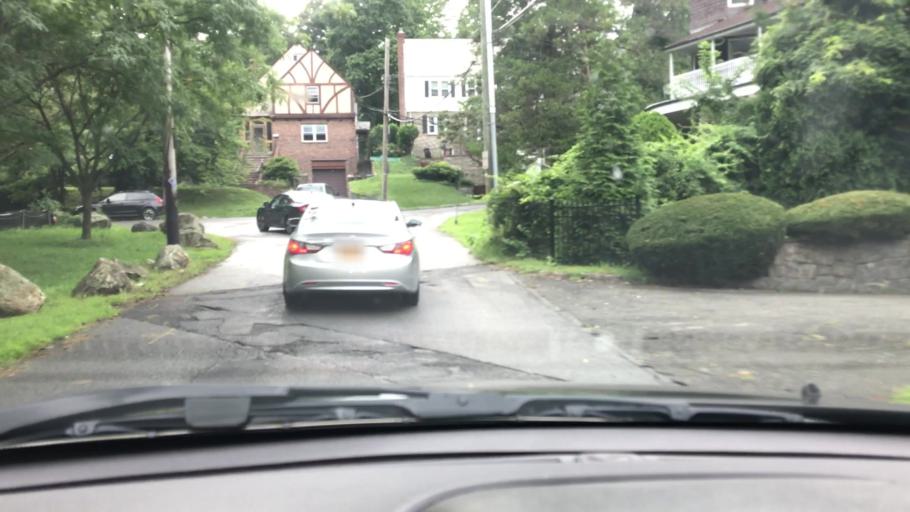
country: US
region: New York
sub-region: Westchester County
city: New Rochelle
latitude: 40.9331
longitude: -73.7918
